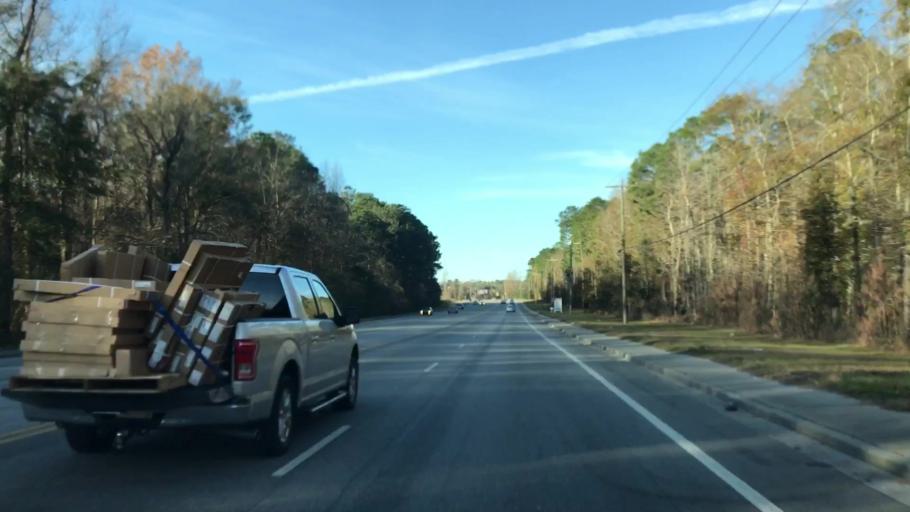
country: US
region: South Carolina
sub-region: Berkeley County
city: Ladson
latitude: 32.9836
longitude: -80.1200
